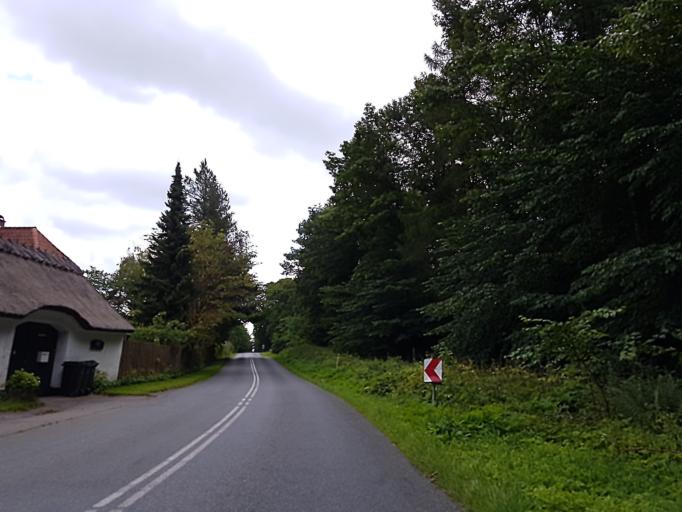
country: DK
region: Capital Region
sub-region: Fureso Kommune
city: Farum
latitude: 55.8093
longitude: 12.3237
